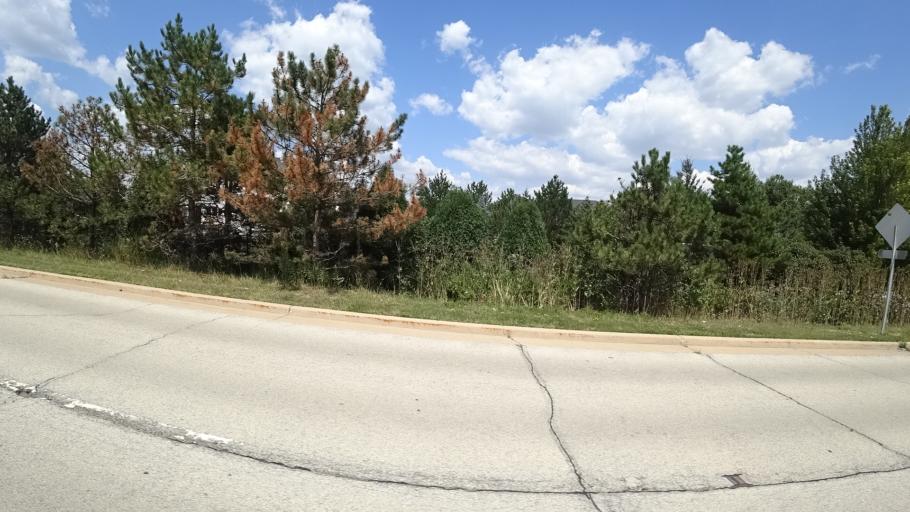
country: US
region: Illinois
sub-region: Cook County
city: Palos Heights
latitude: 41.6313
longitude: -87.8102
